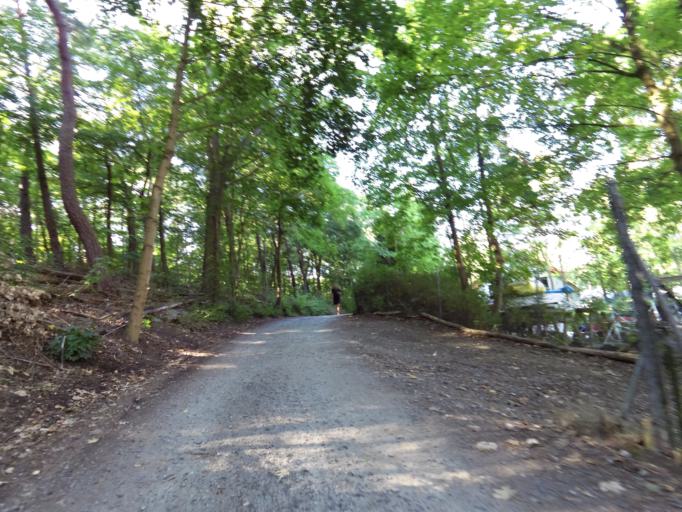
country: DE
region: Berlin
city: Nikolassee
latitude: 52.4457
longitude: 13.1776
